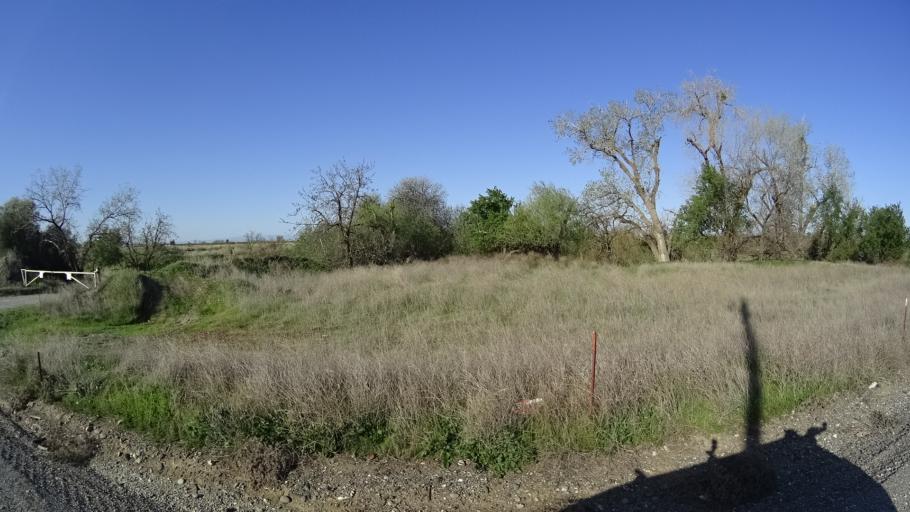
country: US
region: California
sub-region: Glenn County
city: Hamilton City
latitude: 39.7506
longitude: -122.1003
